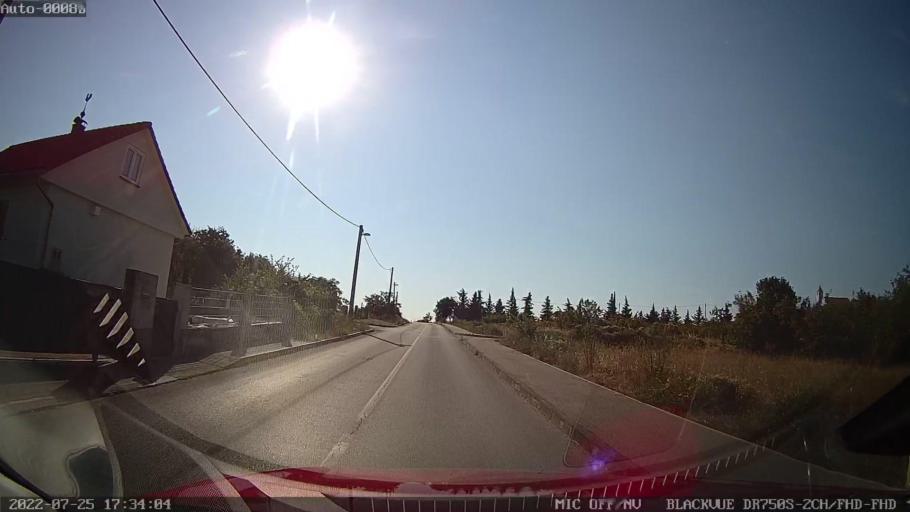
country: HR
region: Zadarska
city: Posedarje
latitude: 44.1828
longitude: 15.4809
